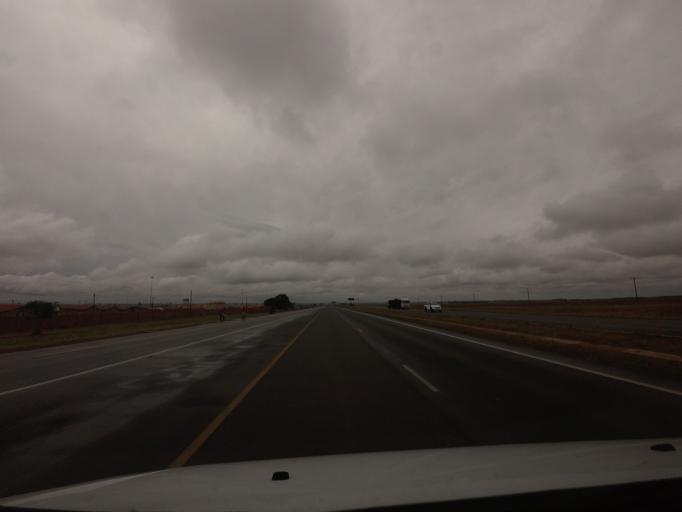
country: ZA
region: Mpumalanga
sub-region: Nkangala District Municipality
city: Middelburg
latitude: -25.8292
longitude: 29.5320
